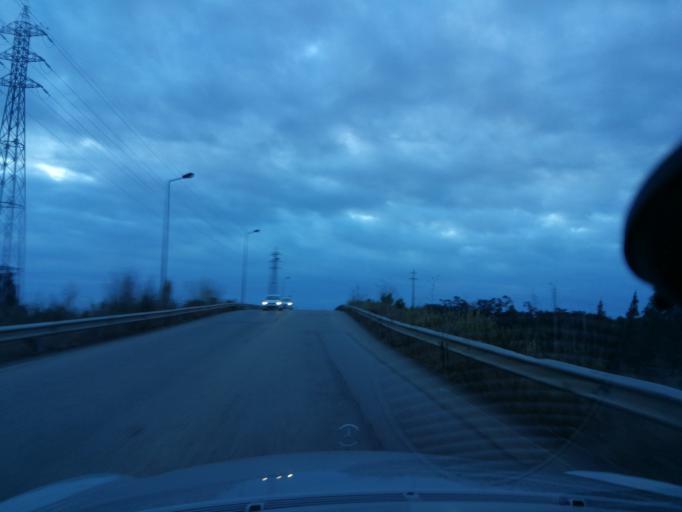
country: PT
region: Aveiro
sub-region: Estarreja
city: Estarreja
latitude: 40.7687
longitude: -8.5765
